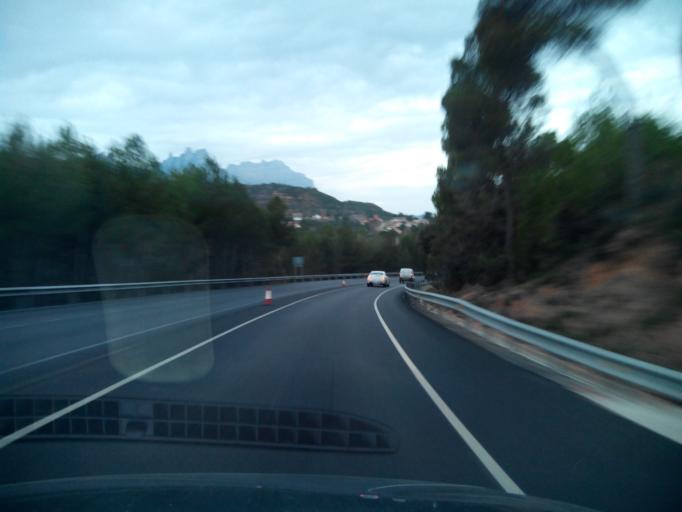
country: ES
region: Catalonia
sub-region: Provincia de Barcelona
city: Olesa de Montserrat
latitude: 41.5909
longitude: 1.9005
